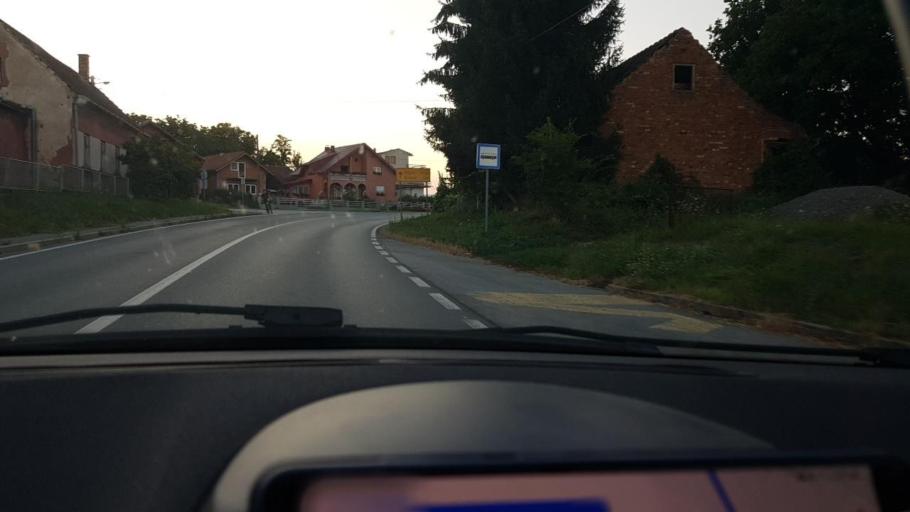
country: HR
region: Bjelovarsko-Bilogorska
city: Zdralovi
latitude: 45.8630
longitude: 16.9194
